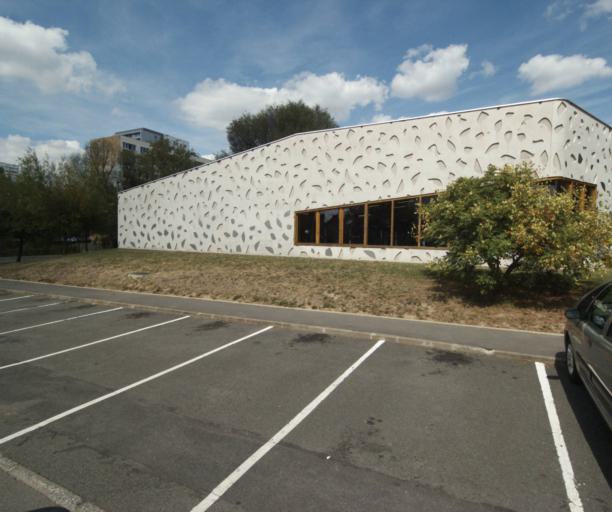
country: FR
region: Nord-Pas-de-Calais
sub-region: Departement du Nord
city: Mons-en-Baroeul
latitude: 50.6404
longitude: 3.1153
